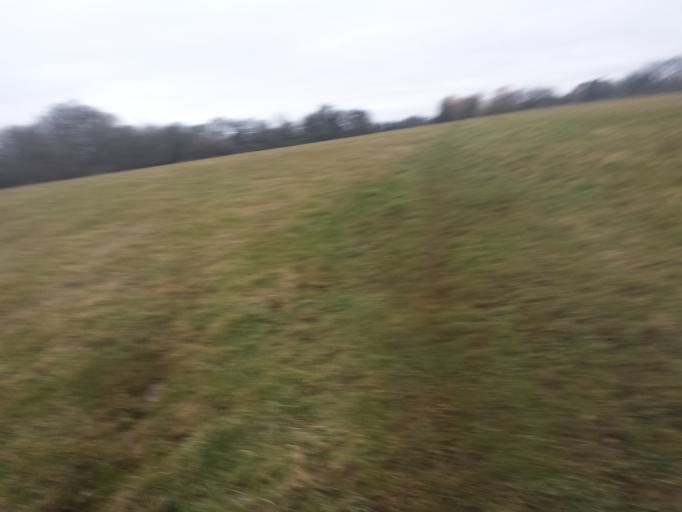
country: GB
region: England
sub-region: Essex
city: Little Clacton
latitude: 51.8451
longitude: 1.1466
